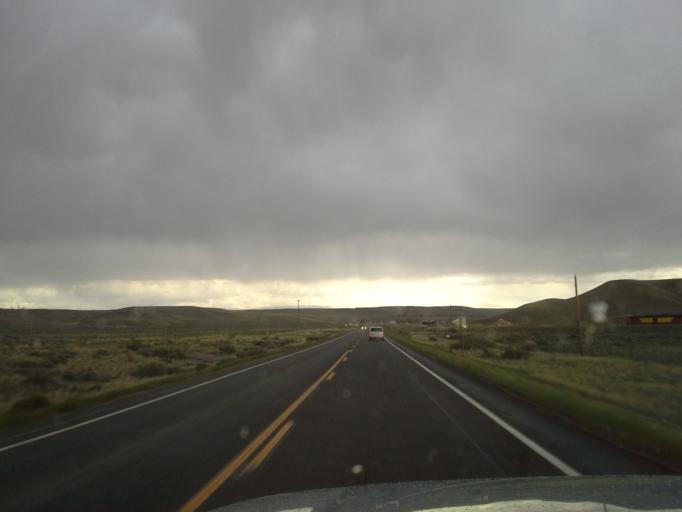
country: US
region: Wyoming
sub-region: Park County
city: Powell
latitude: 45.0659
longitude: -108.6706
